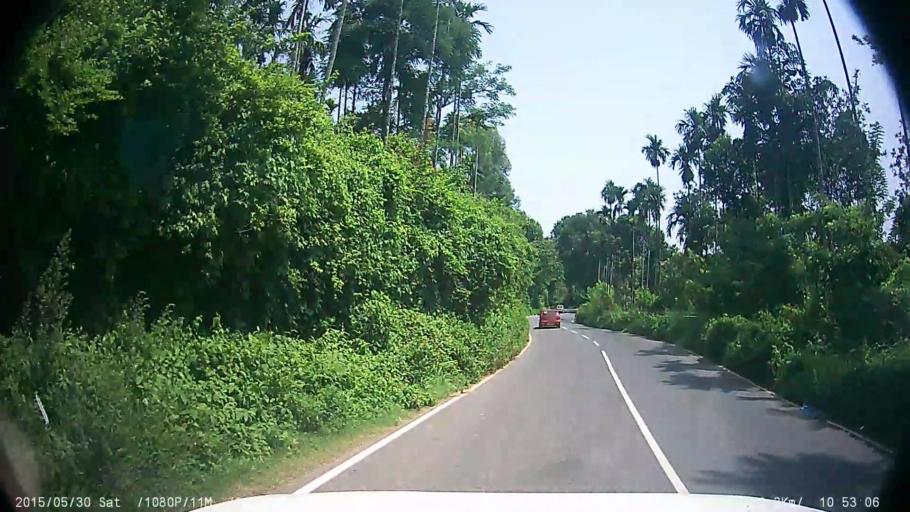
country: IN
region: Kerala
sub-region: Wayanad
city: Kalpetta
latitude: 11.6563
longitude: 76.0877
